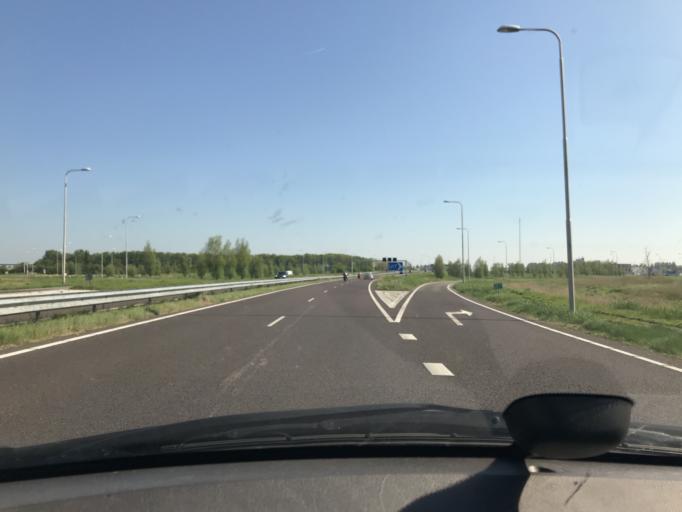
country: NL
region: Zeeland
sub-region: Gemeente Middelburg
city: Middelburg
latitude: 51.5106
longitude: 3.6323
